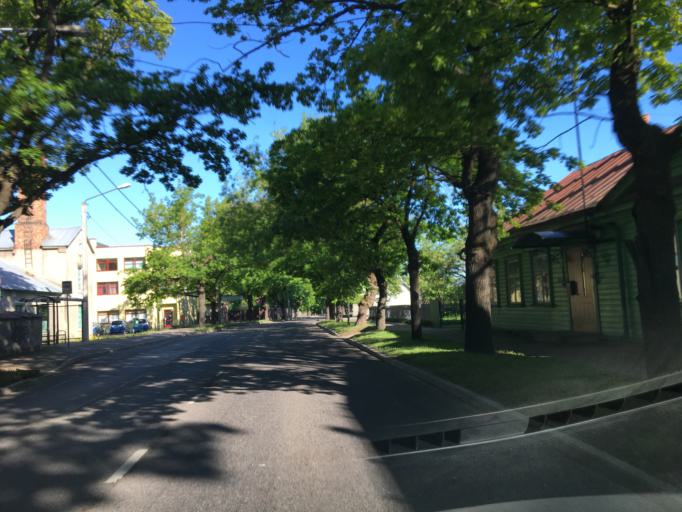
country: EE
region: Tartu
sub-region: Tartu linn
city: Tartu
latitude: 58.3932
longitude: 26.7186
